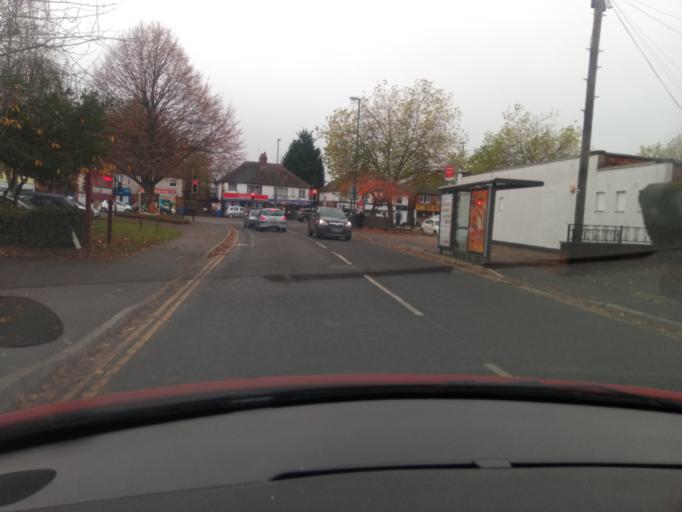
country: GB
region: England
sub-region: Derby
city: Derby
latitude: 52.9247
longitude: -1.4379
